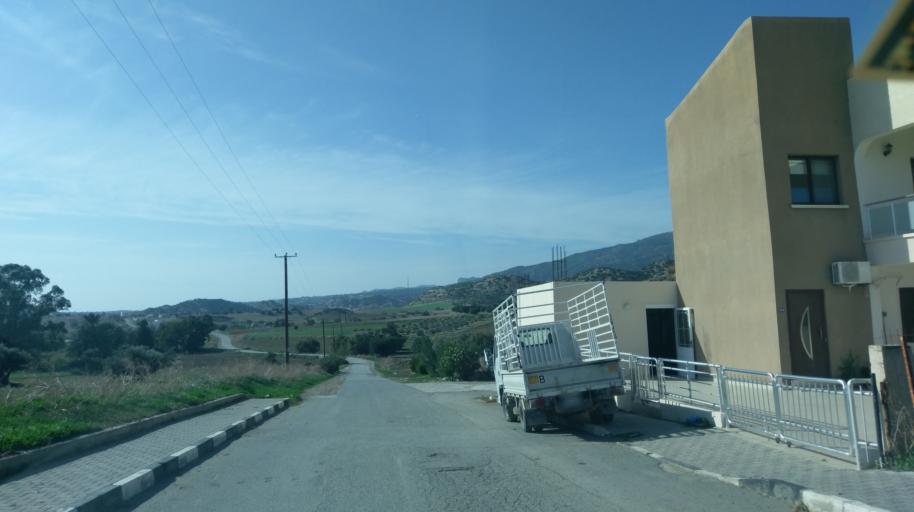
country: CY
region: Ammochostos
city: Trikomo
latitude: 35.3655
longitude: 33.9362
